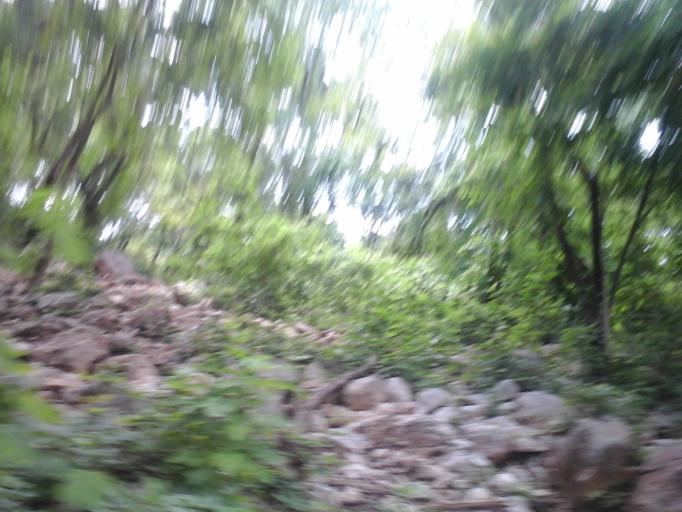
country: CO
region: Cesar
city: Becerril
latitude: 9.7491
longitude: -73.1580
